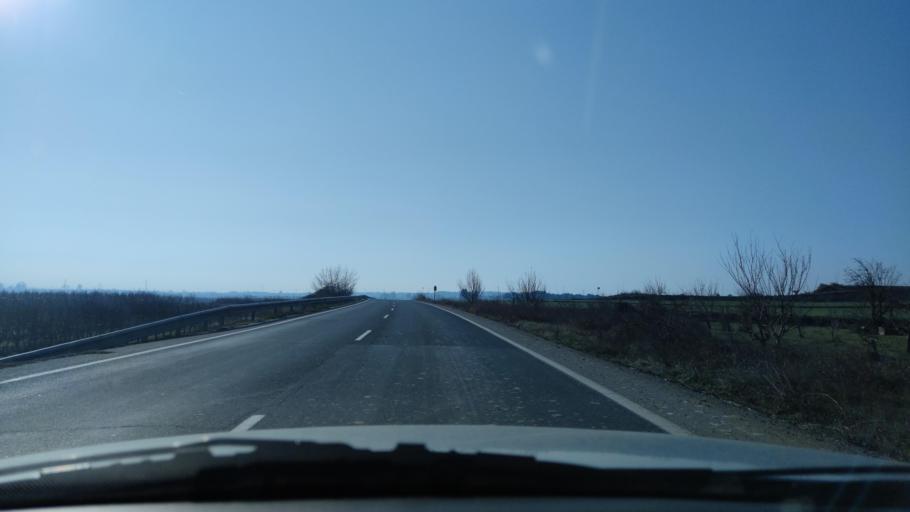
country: ES
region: Catalonia
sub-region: Provincia de Lleida
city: Albesa
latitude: 41.7221
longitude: 0.6401
